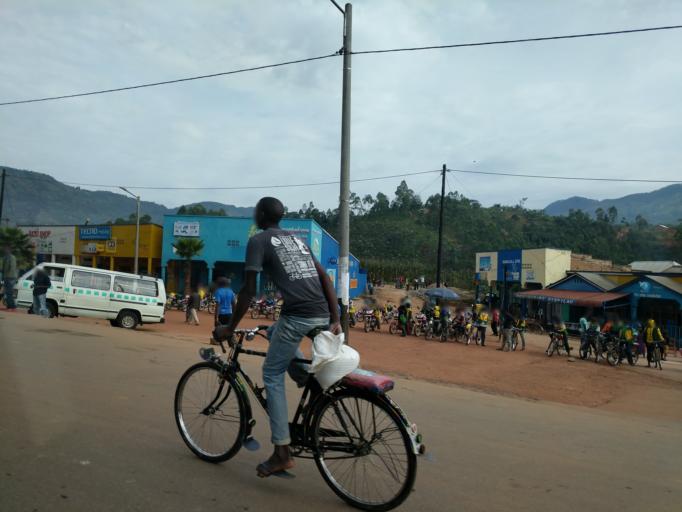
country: RW
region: Northern Province
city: Musanze
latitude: -1.6471
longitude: 29.7905
